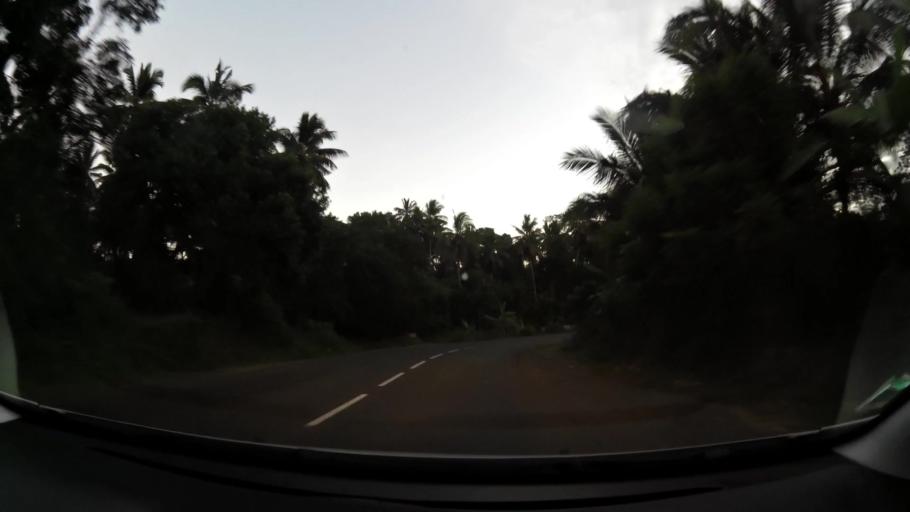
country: YT
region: Bandraboua
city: Bandraboua
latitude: -12.7309
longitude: 45.1312
